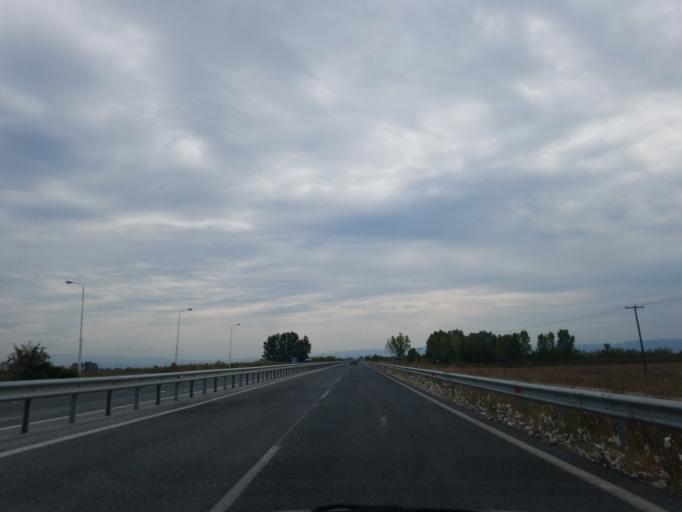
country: GR
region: Thessaly
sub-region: Nomos Kardhitsas
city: Sofades
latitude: 39.3158
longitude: 22.1157
